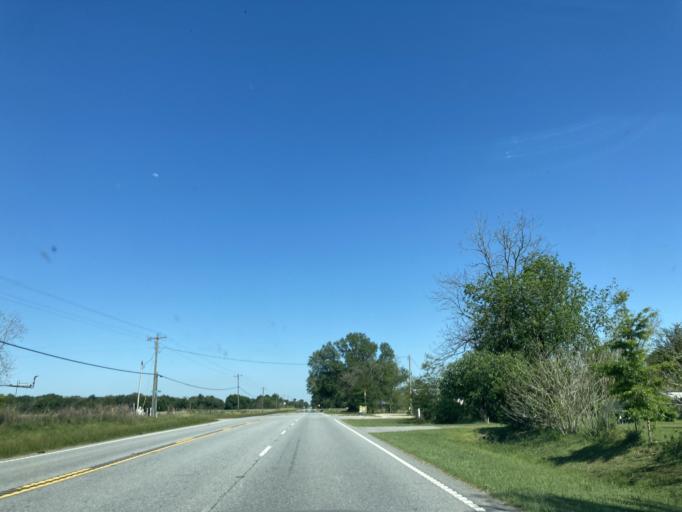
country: US
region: Georgia
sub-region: Miller County
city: Colquitt
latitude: 31.1850
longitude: -84.5942
